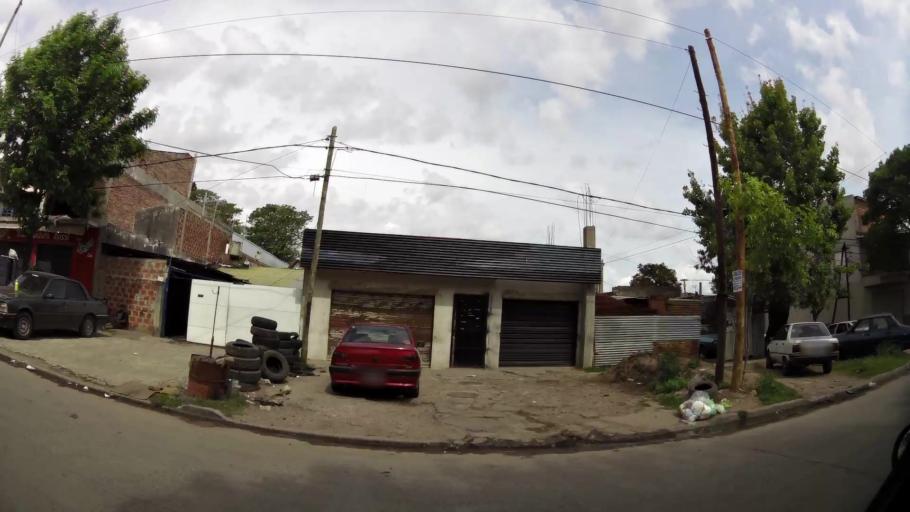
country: AR
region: Buenos Aires
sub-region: Partido de Quilmes
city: Quilmes
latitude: -34.7553
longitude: -58.2502
